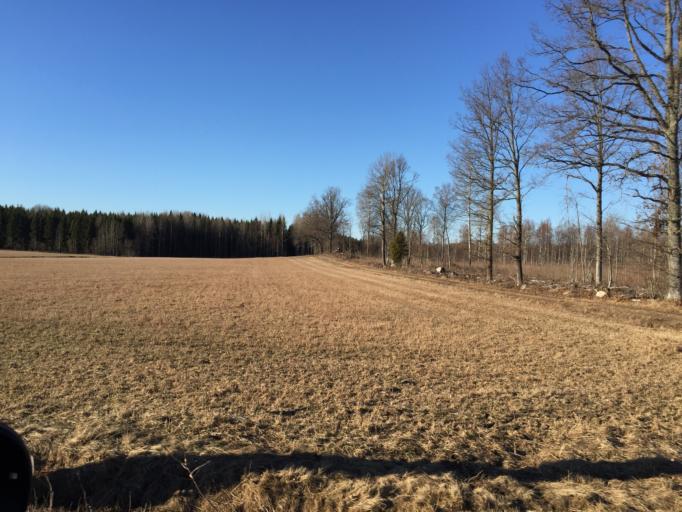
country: SE
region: Soedermanland
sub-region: Vingakers Kommun
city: Vingaker
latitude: 59.0393
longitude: 15.7269
